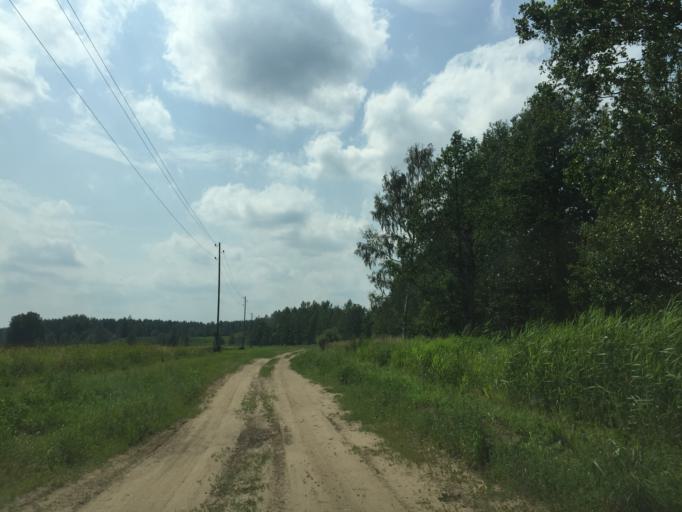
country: LV
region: Olaine
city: Olaine
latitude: 56.7752
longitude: 23.9174
